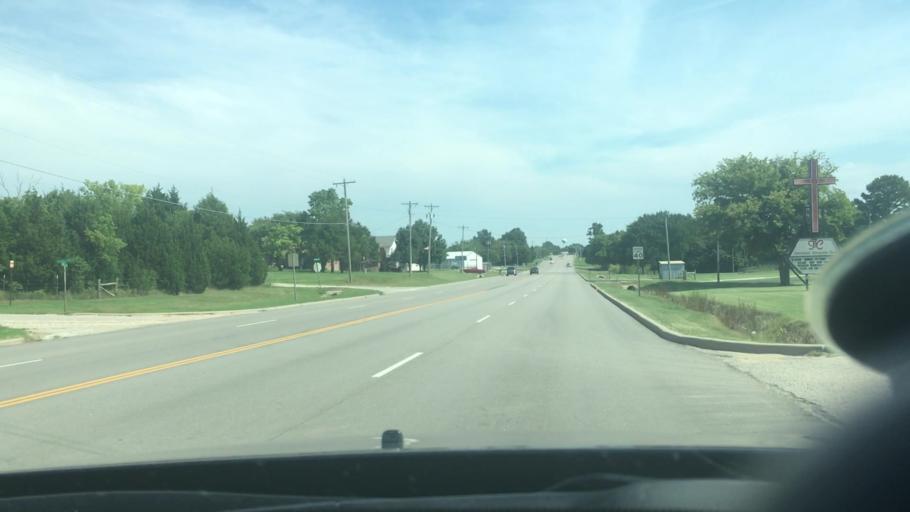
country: US
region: Oklahoma
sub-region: Seminole County
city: Seminole
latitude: 35.2539
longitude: -96.7070
